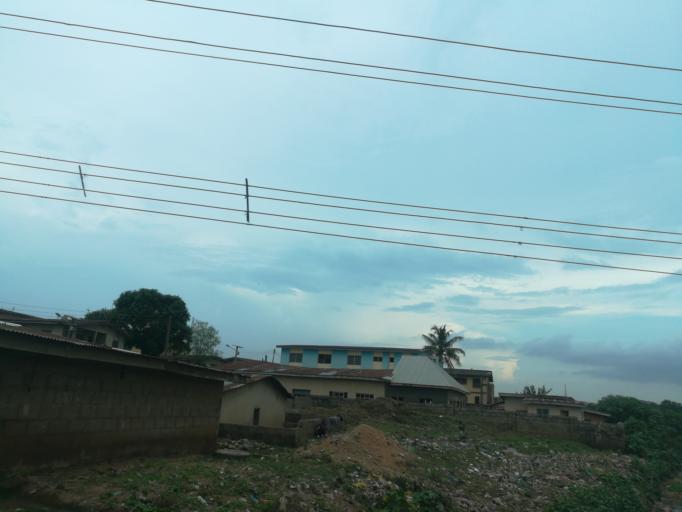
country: NG
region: Oyo
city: Ibadan
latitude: 7.4467
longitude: 3.9136
